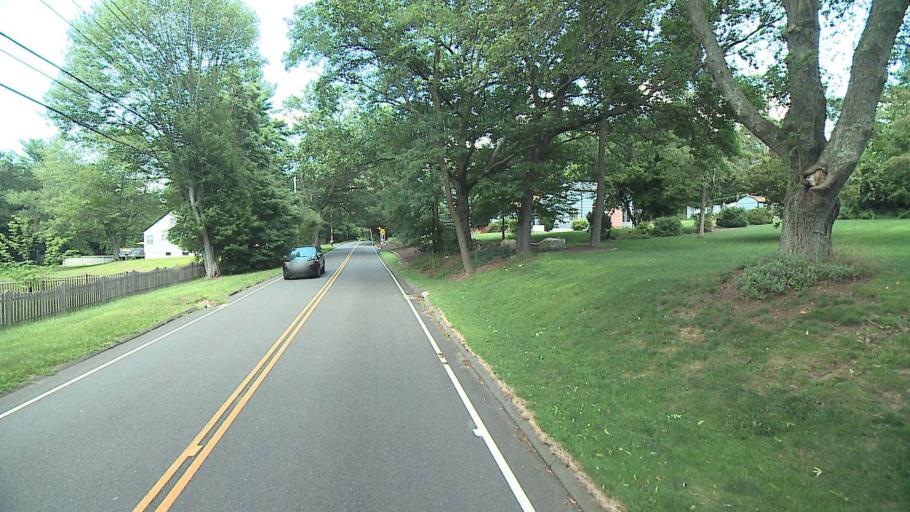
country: US
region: Connecticut
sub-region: Fairfield County
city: Trumbull
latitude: 41.2775
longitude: -73.1598
